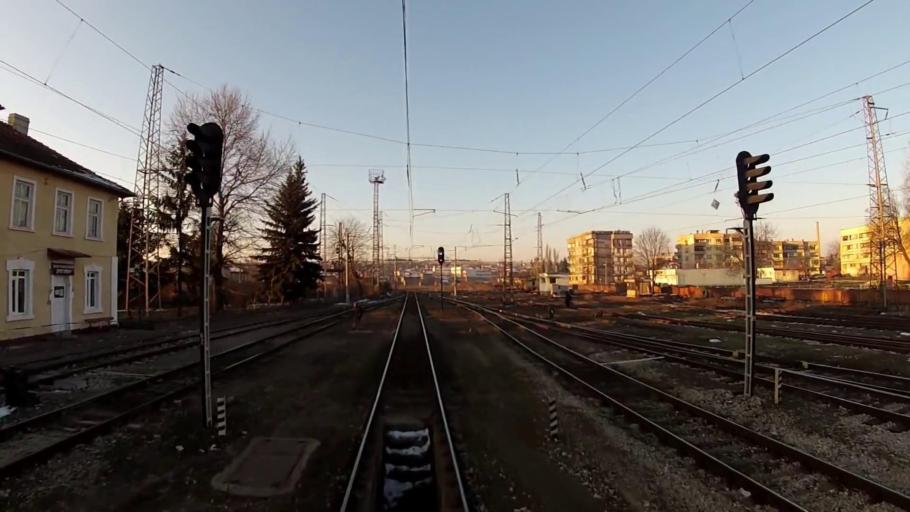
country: BG
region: Sofiya
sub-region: Obshtina Dragoman
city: Dragoman
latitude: 42.9184
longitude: 22.9303
